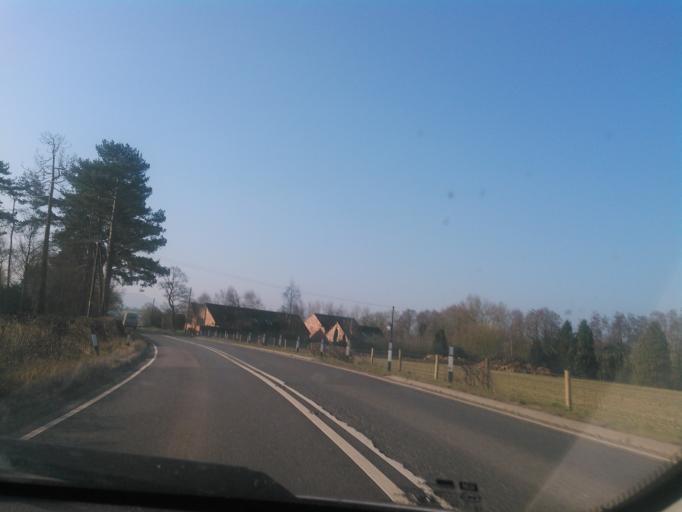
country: GB
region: England
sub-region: Shropshire
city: Craven Arms
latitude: 52.4833
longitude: -2.8183
